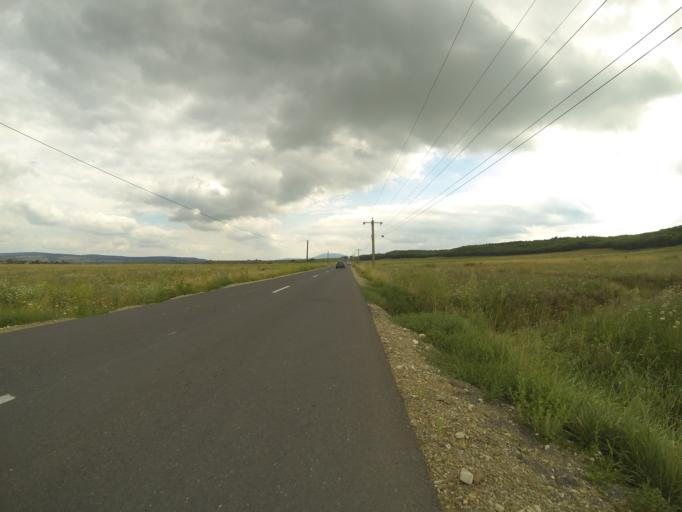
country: RO
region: Brasov
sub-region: Comuna Sercaia
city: Sercaia
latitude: 45.8342
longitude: 25.1558
